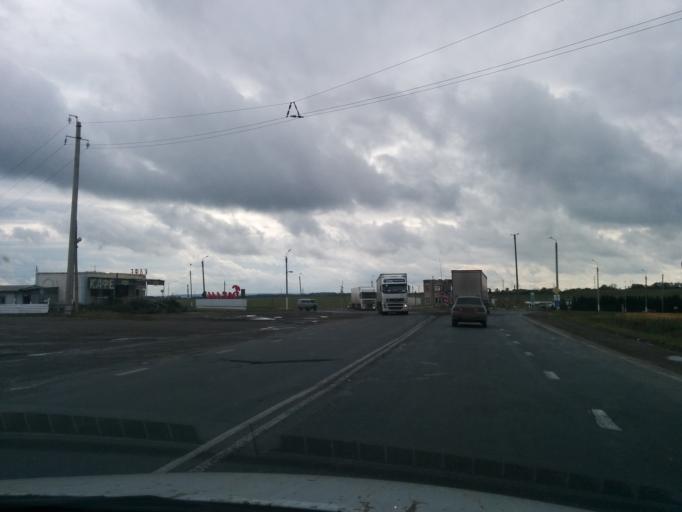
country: RU
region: Tatarstan
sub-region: Bavlinskiy Rayon
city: Bavly
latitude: 54.4238
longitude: 53.1597
